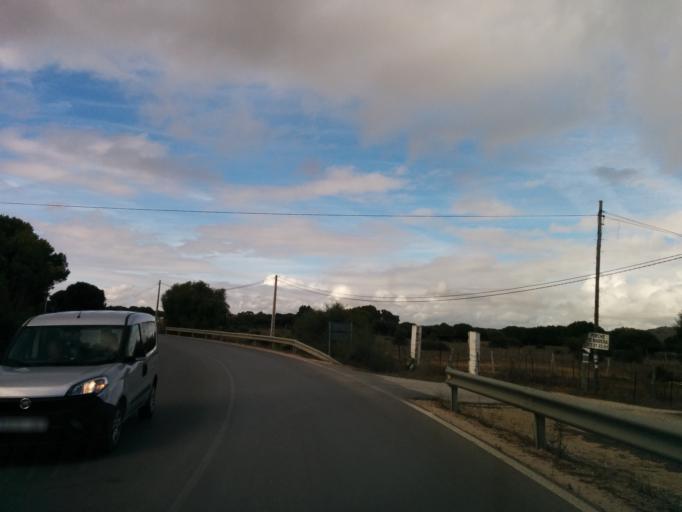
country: ES
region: Andalusia
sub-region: Provincia de Cadiz
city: Vejer de la Frontera
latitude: 36.2048
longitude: -6.0340
